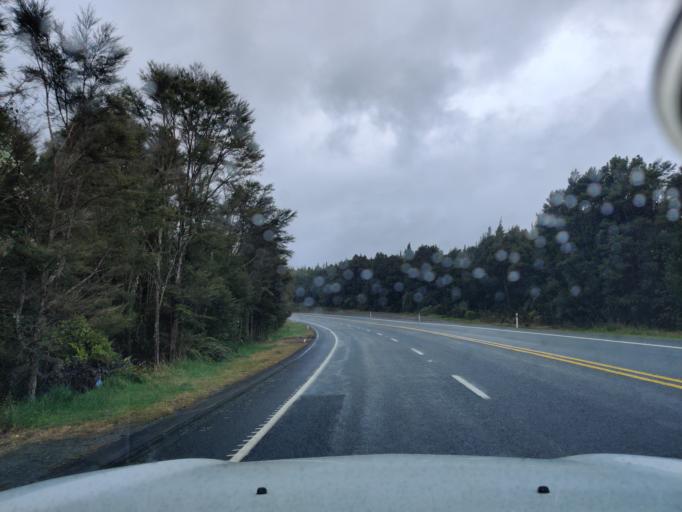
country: NZ
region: Waikato
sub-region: South Waikato District
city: Tokoroa
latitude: -38.0192
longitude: 175.9548
